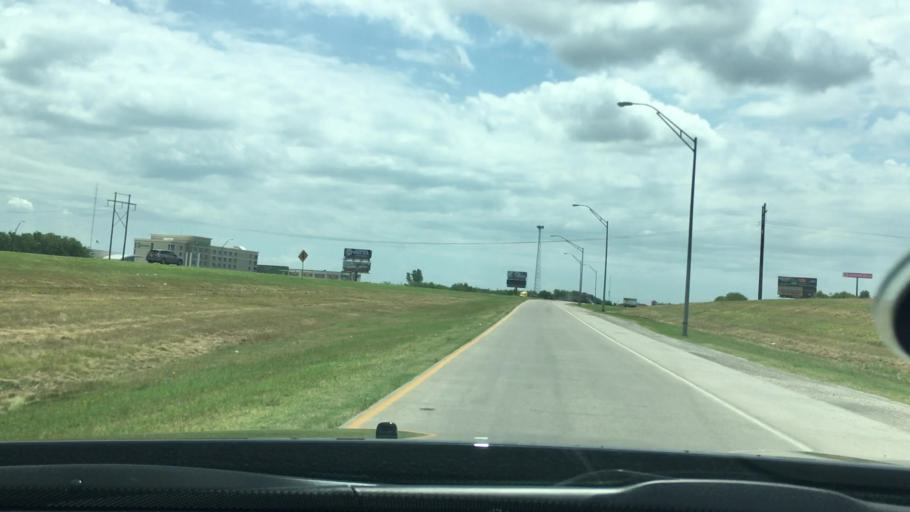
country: US
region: Oklahoma
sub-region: Carter County
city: Ardmore
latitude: 34.2011
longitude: -97.1650
